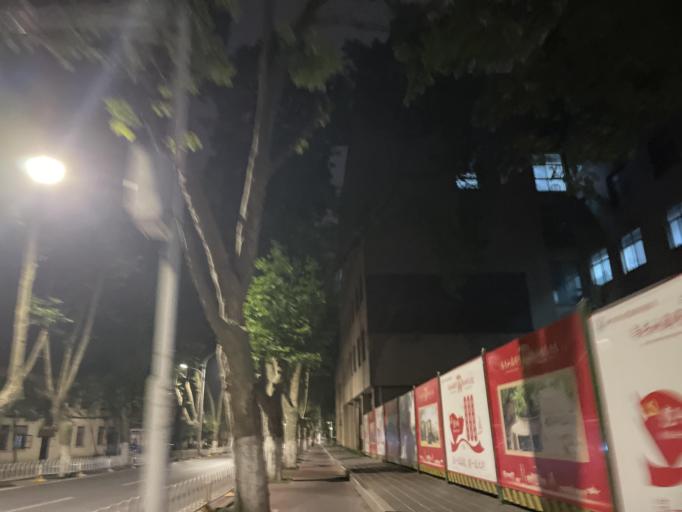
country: CN
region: Hubei
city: Guanshan
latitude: 30.5181
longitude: 114.4108
